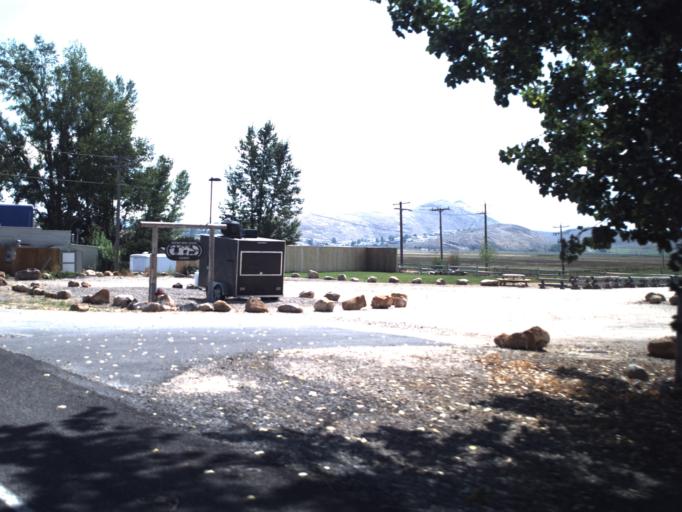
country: US
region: Utah
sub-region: Rich County
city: Randolph
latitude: 41.9082
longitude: -111.3867
